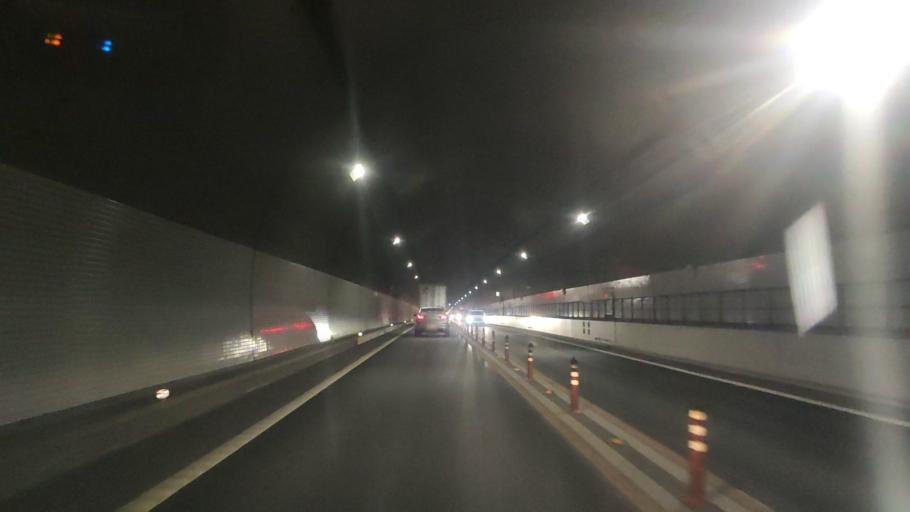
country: JP
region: Fukuoka
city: Kanda
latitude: 33.7636
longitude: 130.9626
